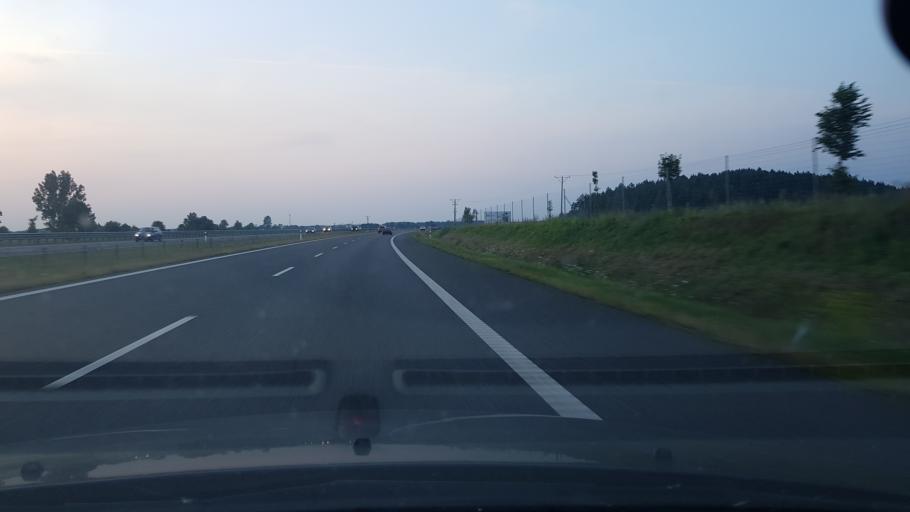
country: PL
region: Warmian-Masurian Voivodeship
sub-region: Powiat nidzicki
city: Nidzica
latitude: 53.4223
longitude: 20.3362
